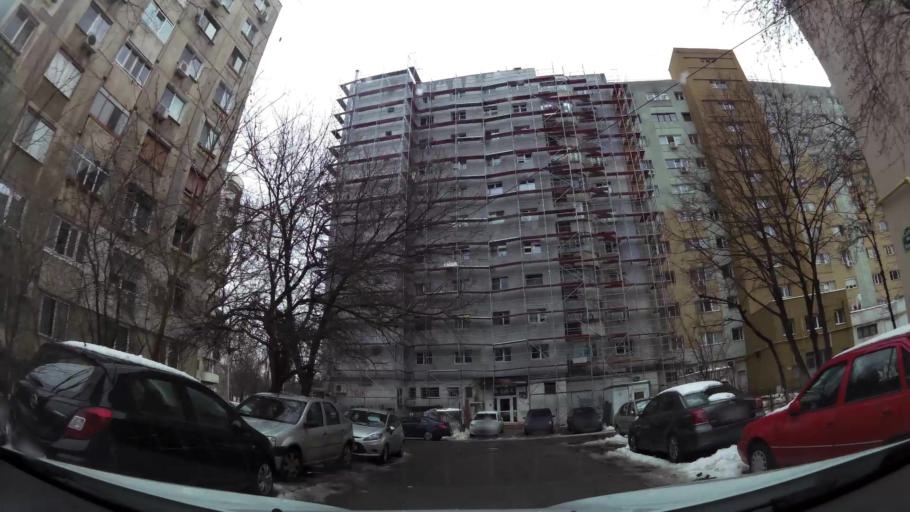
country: RO
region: Bucuresti
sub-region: Municipiul Bucuresti
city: Bucuresti
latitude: 44.4161
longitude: 26.0488
